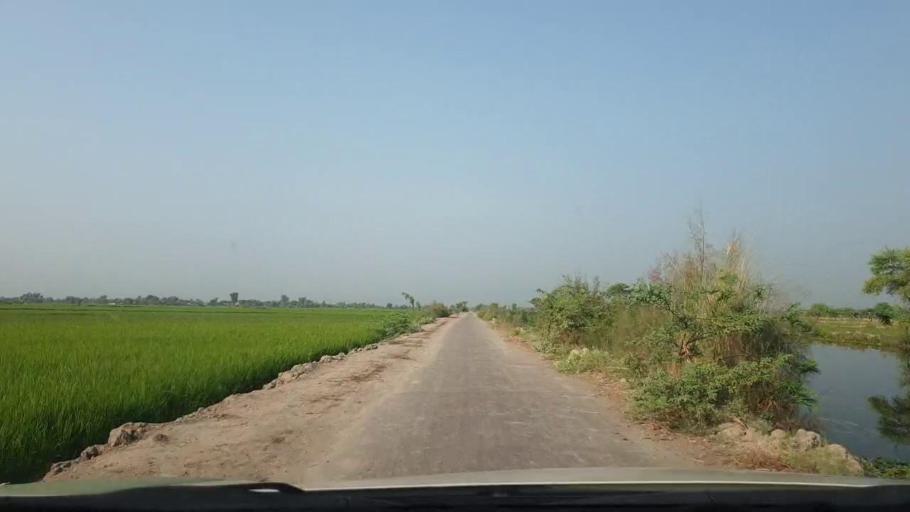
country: PK
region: Sindh
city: Larkana
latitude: 27.5006
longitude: 68.1752
